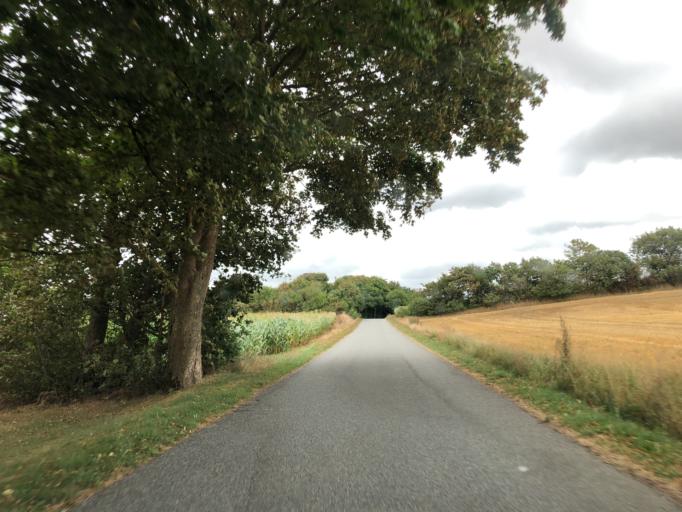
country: DK
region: Central Jutland
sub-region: Ringkobing-Skjern Kommune
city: Videbaek
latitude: 56.1059
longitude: 8.4904
